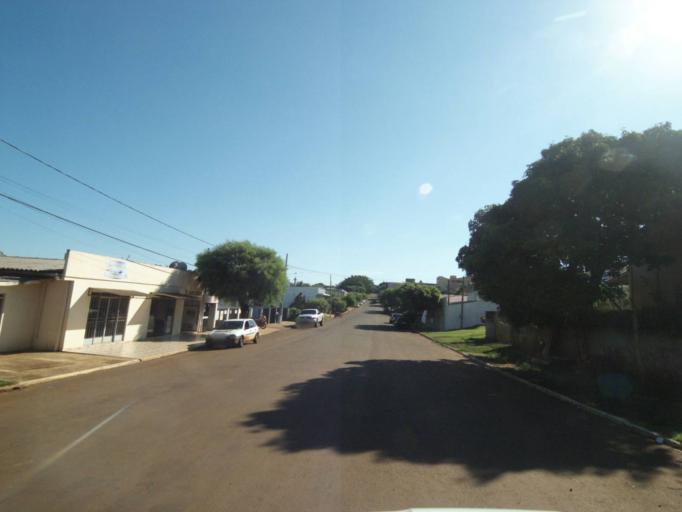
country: BR
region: Parana
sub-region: Laranjeiras Do Sul
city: Laranjeiras do Sul
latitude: -25.4908
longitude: -52.5289
